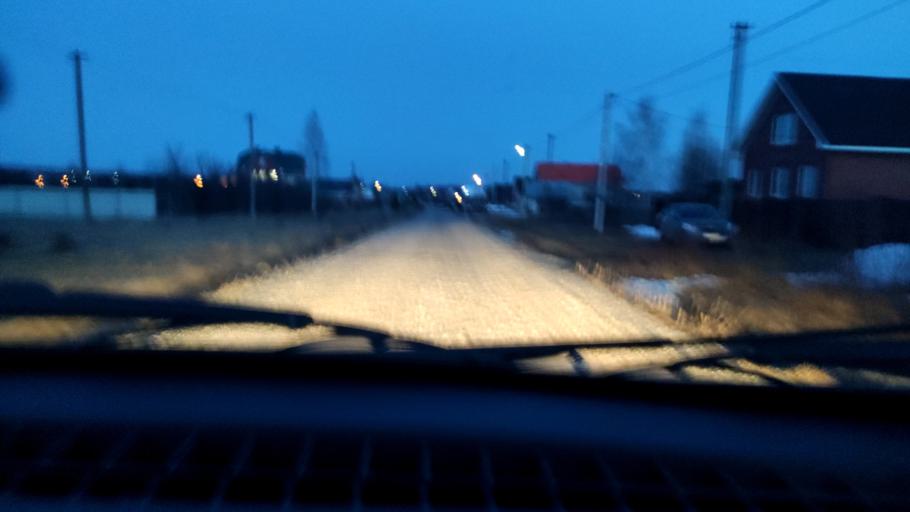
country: RU
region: Bashkortostan
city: Iglino
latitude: 54.7938
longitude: 56.3104
